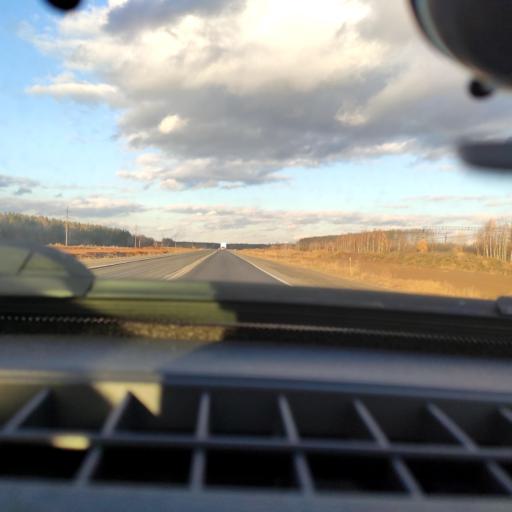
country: RU
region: Bashkortostan
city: Kabakovo
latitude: 54.7084
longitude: 56.2241
